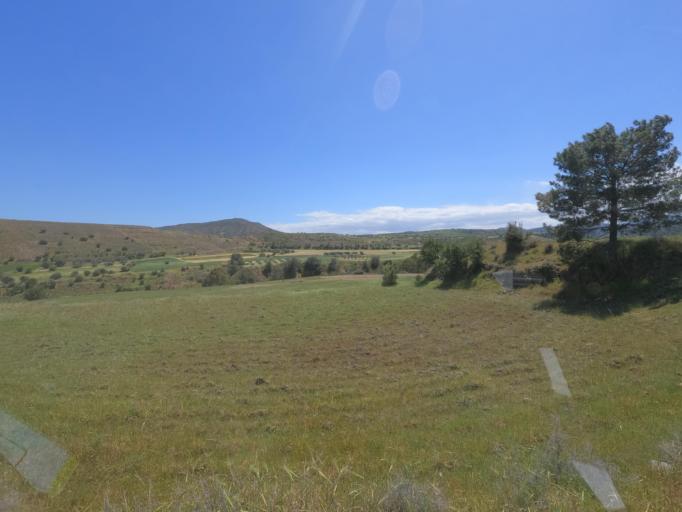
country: CY
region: Lefkosia
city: Peristerona
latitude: 35.0569
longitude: 33.0761
